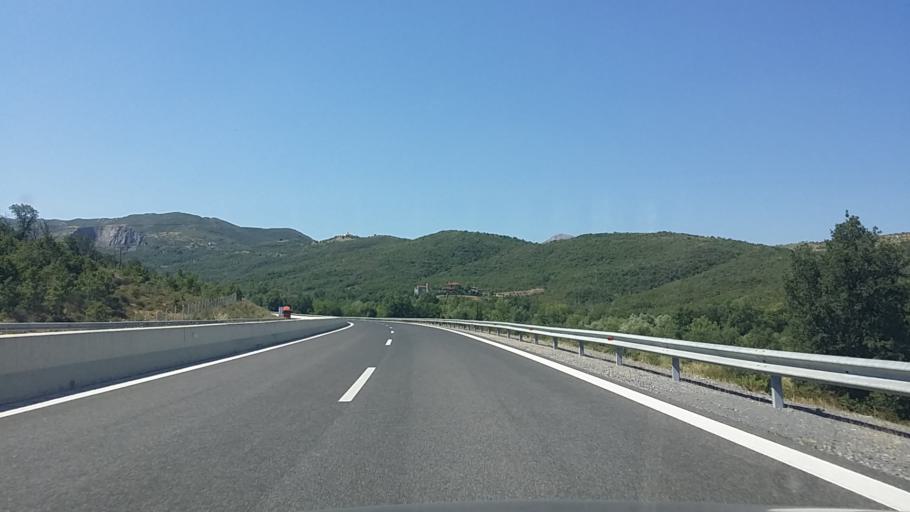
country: GR
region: Peloponnese
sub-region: Nomos Arkadias
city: Megalopoli
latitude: 37.3431
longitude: 22.1528
